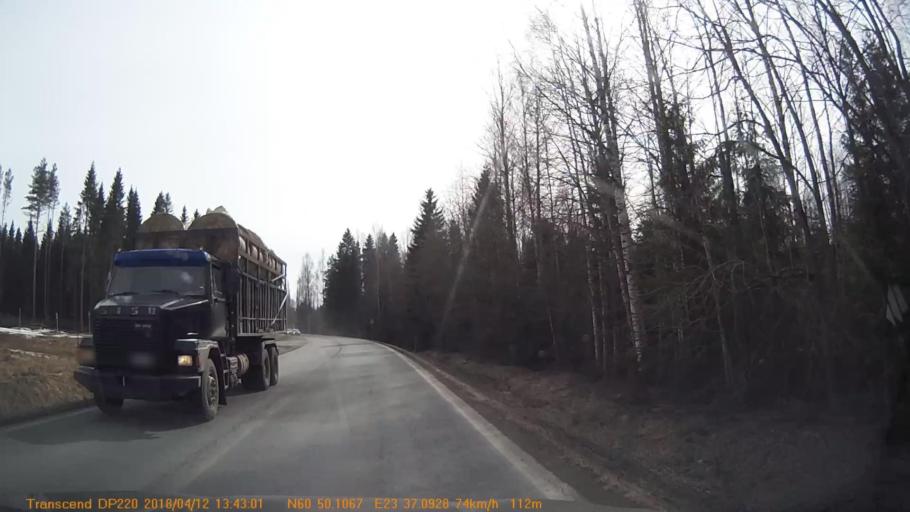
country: FI
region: Haeme
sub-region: Forssa
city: Forssa
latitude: 60.8345
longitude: 23.6183
